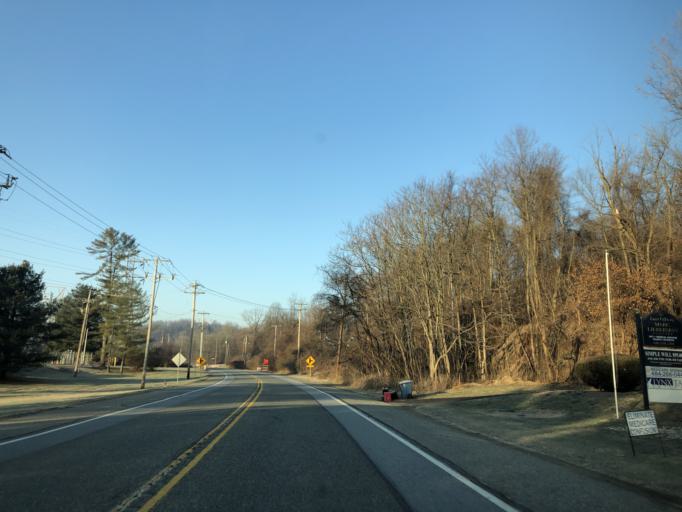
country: US
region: Pennsylvania
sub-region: Chester County
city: Downingtown
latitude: 39.9699
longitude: -75.6666
